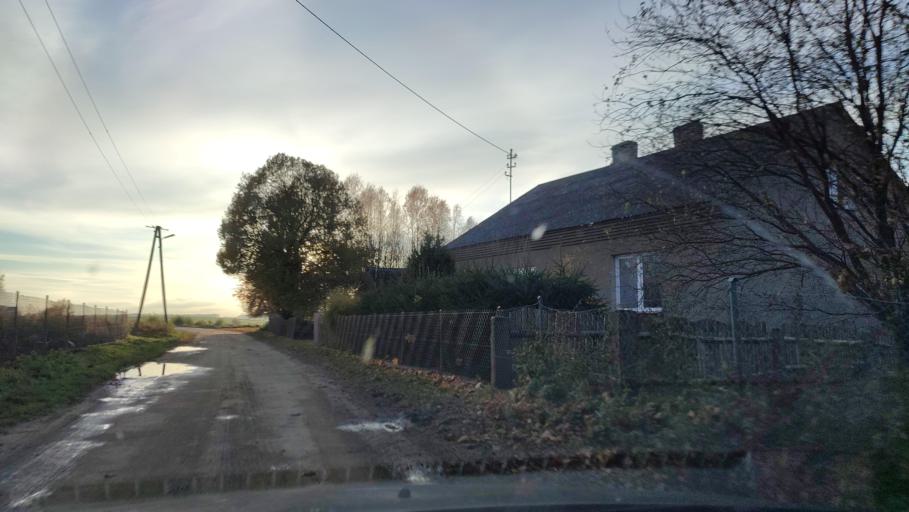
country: PL
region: Masovian Voivodeship
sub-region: Powiat mlawski
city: Dzierzgowo
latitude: 53.2755
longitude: 20.6484
